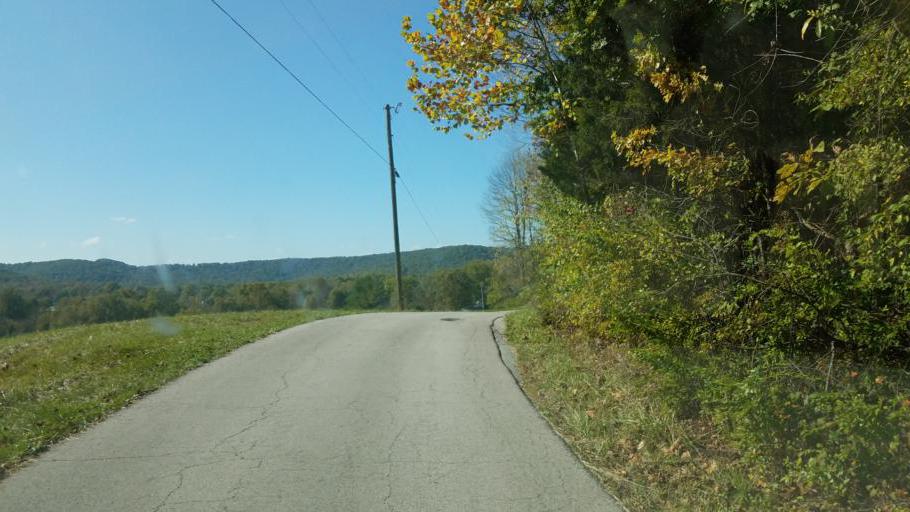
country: US
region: Kentucky
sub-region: Fleming County
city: Flemingsburg
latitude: 38.4448
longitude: -83.5701
